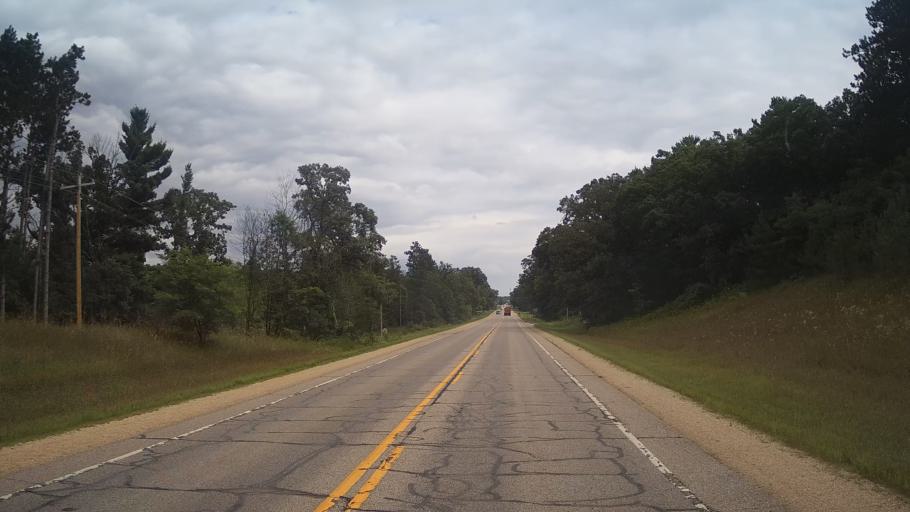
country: US
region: Wisconsin
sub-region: Waushara County
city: Wautoma
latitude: 44.0684
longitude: -89.3162
